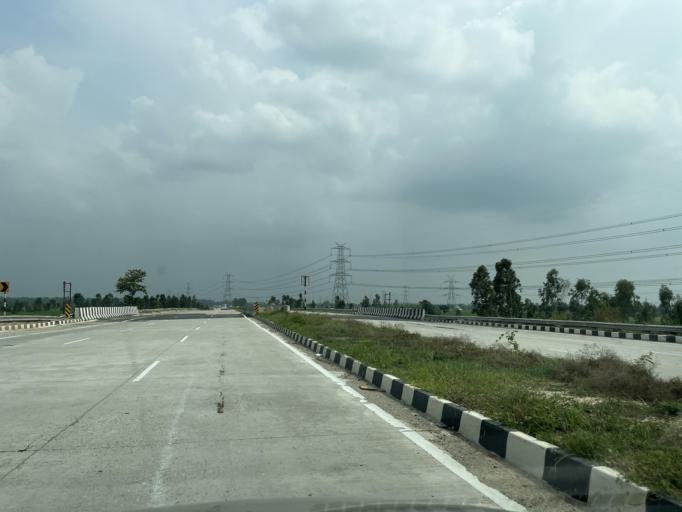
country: IN
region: Uttarakhand
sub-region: Udham Singh Nagar
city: Jaspur
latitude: 29.2887
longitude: 78.8535
